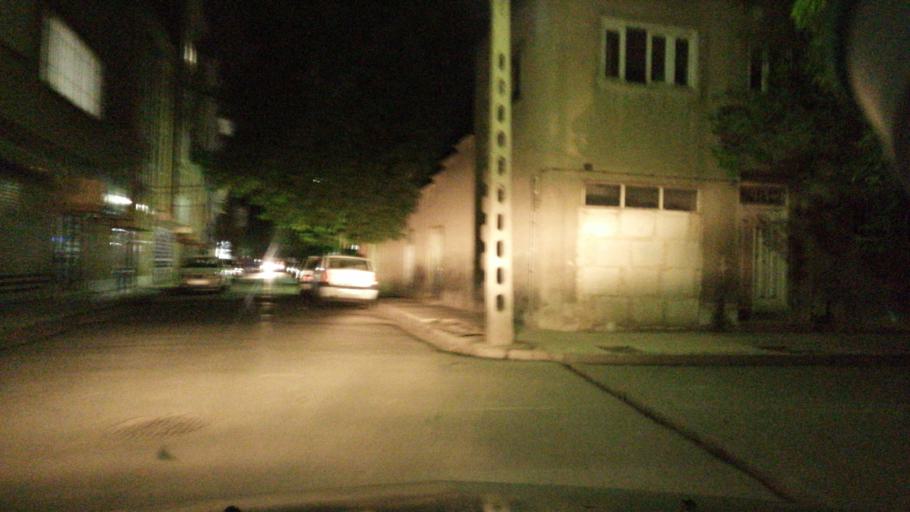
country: IR
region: Razavi Khorasan
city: Mashhad
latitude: 36.3079
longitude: 59.6033
